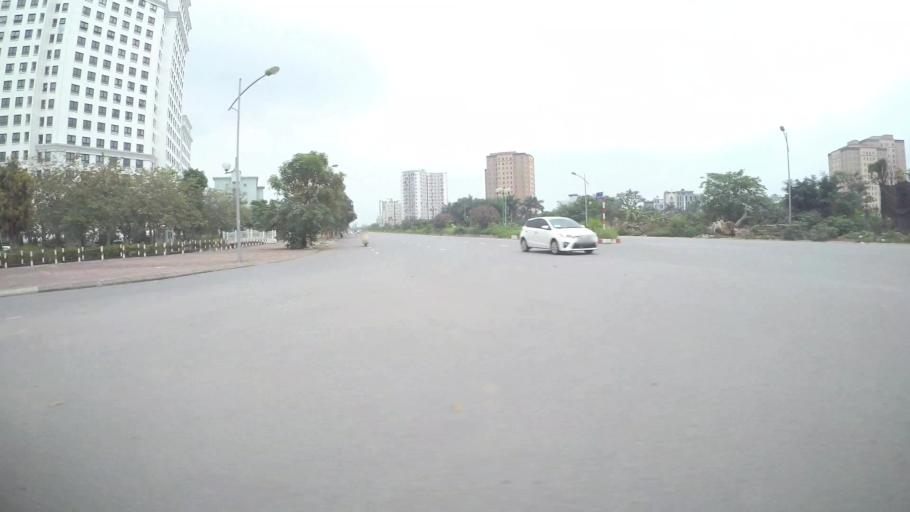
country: VN
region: Ha Noi
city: Trau Quy
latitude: 21.0564
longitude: 105.9134
